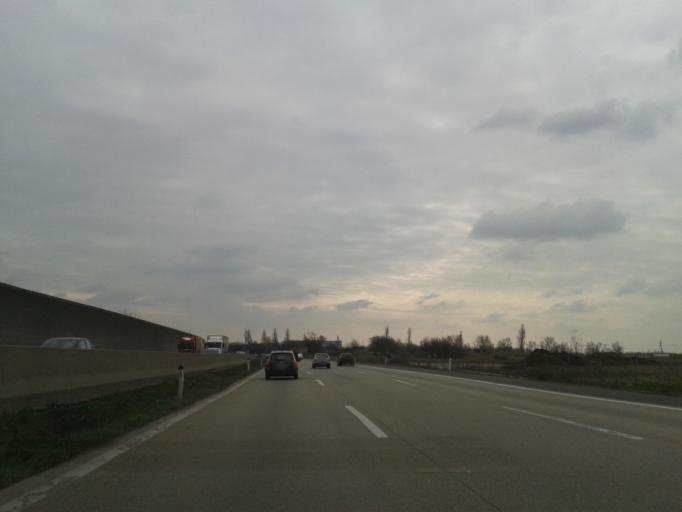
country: AT
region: Lower Austria
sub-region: Politischer Bezirk Wien-Umgebung
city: Rauchenwarth
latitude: 48.1377
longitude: 16.5262
